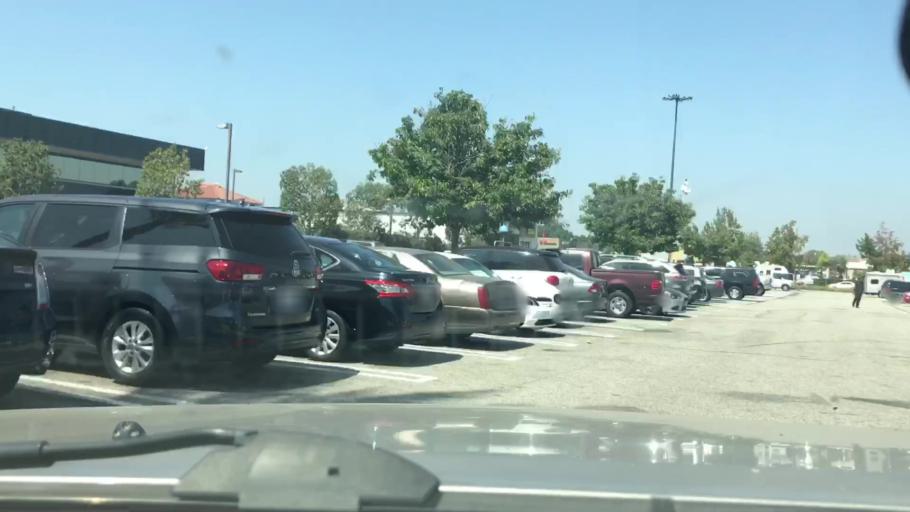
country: US
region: California
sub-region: Los Angeles County
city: Signal Hill
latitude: 33.8310
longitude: -118.1589
